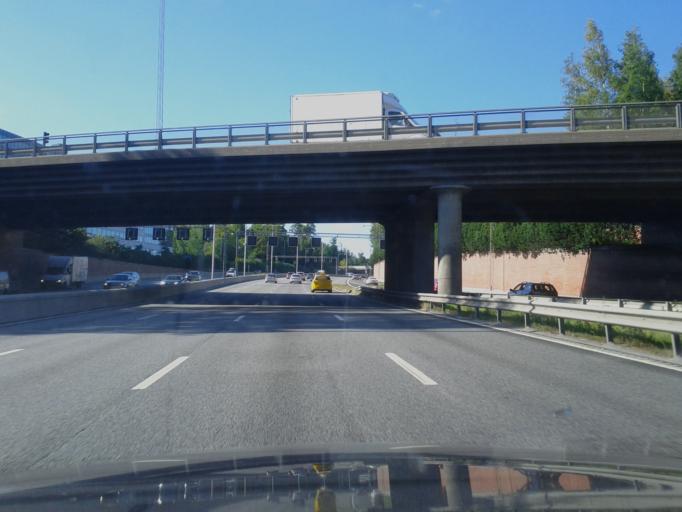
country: SE
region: Stockholm
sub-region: Norrtalje Kommun
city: Bergshamra
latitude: 59.3640
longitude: 18.0238
